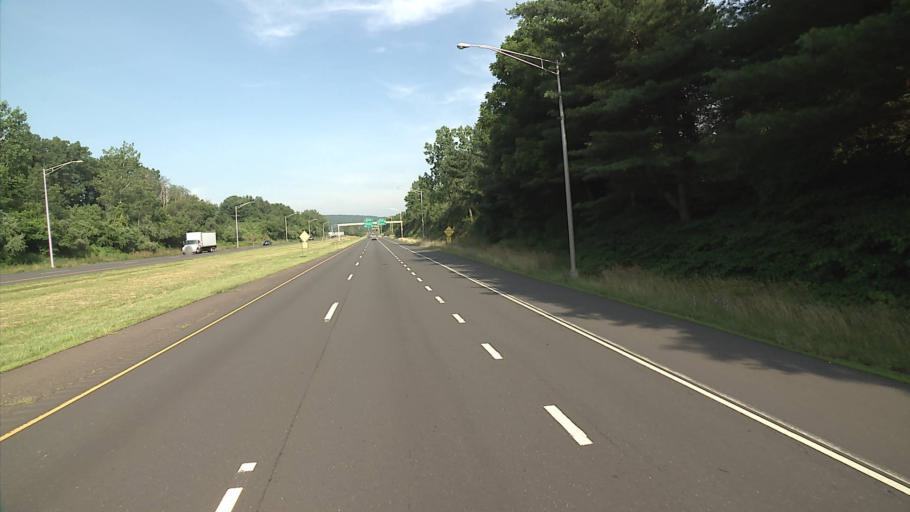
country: US
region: Connecticut
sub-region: New Haven County
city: Cheshire Village
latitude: 41.5586
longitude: -72.9040
